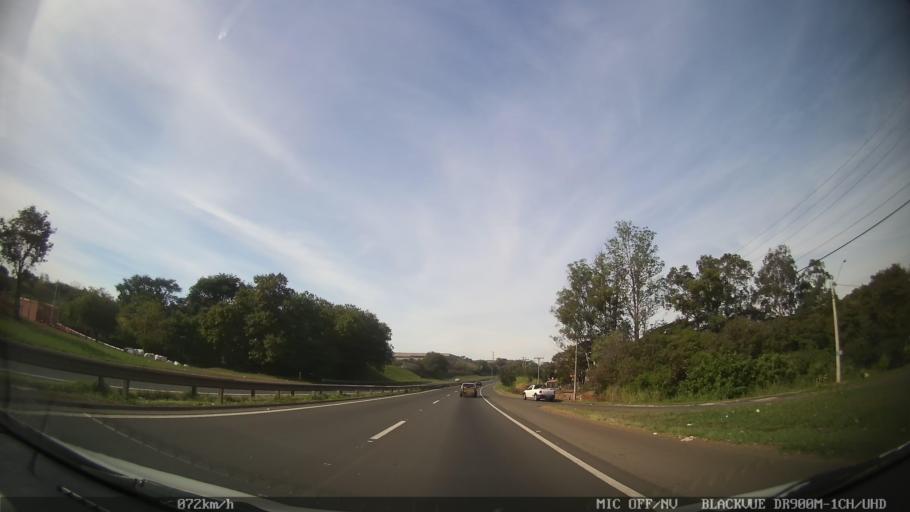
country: BR
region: Sao Paulo
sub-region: Piracicaba
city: Piracicaba
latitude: -22.6887
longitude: -47.6681
